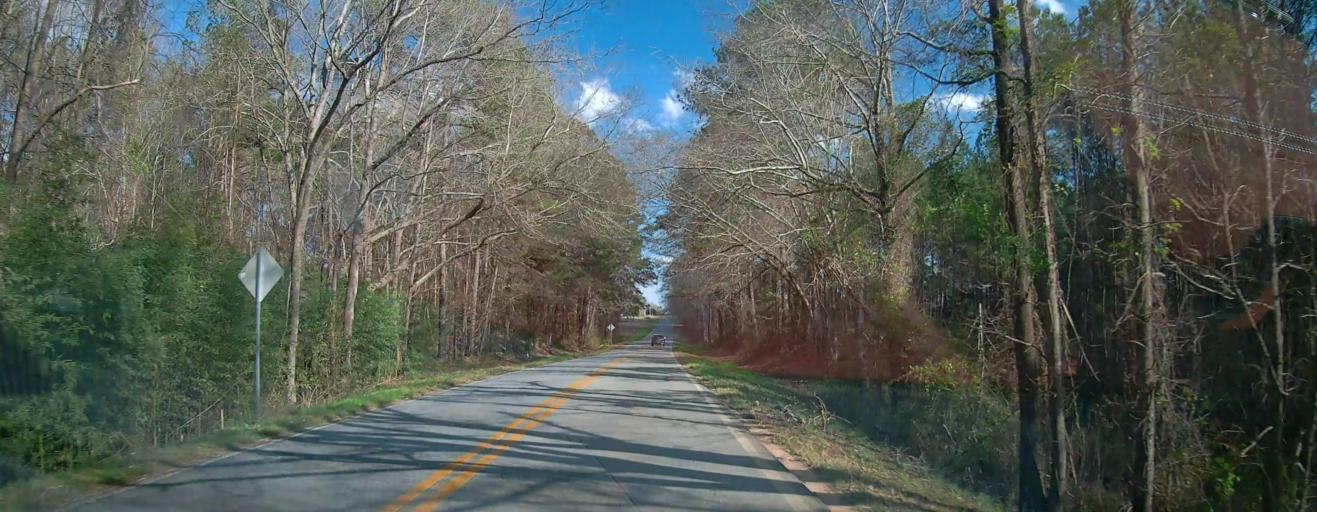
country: US
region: Georgia
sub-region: Laurens County
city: Dublin
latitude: 32.5680
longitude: -83.0312
